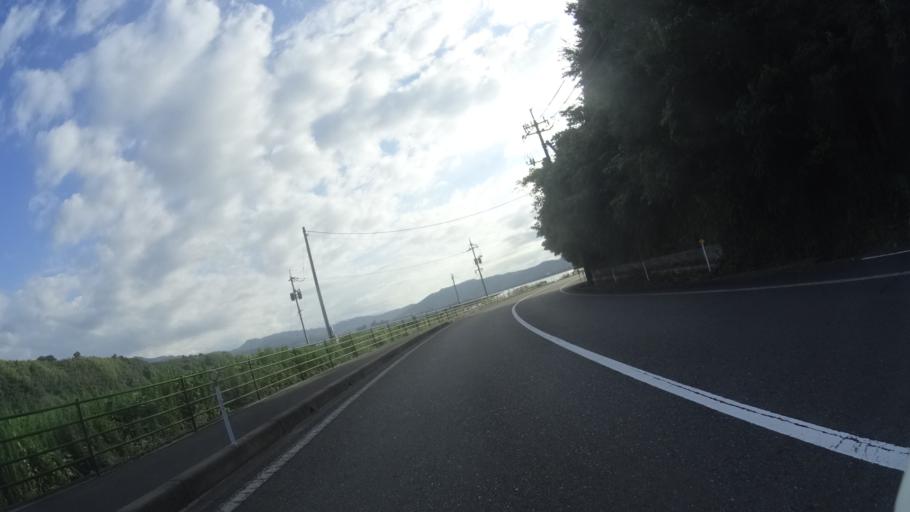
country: JP
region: Tottori
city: Kurayoshi
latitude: 35.4924
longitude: 133.8954
